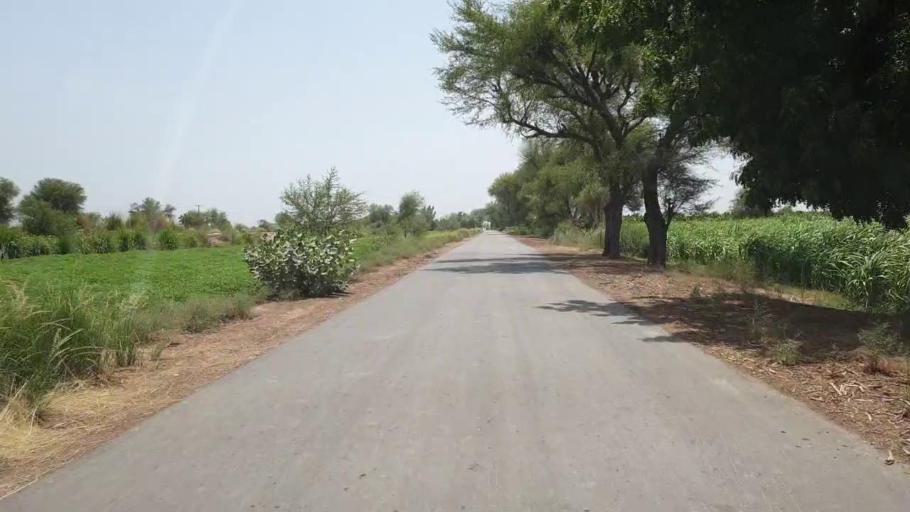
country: PK
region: Sindh
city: Daur
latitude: 26.3934
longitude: 68.2027
